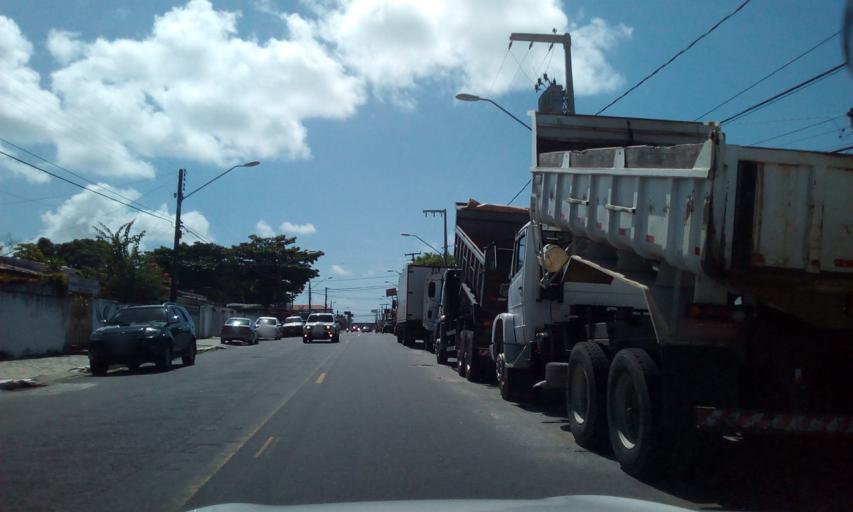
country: BR
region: Paraiba
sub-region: Joao Pessoa
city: Joao Pessoa
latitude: -7.1860
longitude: -34.8433
